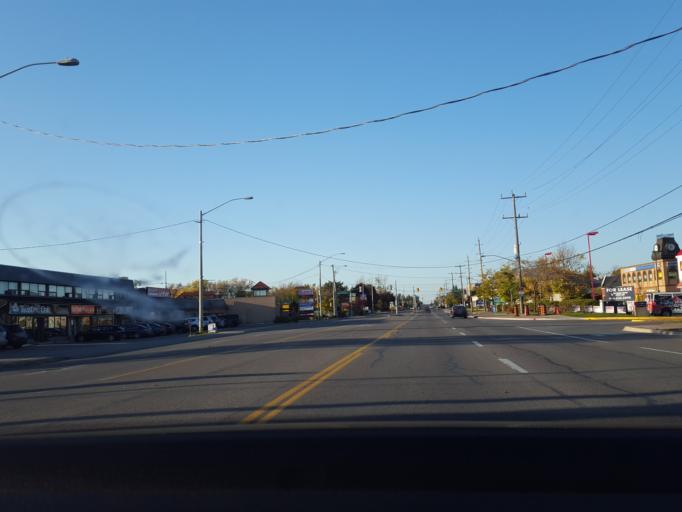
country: CA
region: Ontario
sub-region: York
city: Richmond Hill
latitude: 43.9470
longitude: -79.4552
